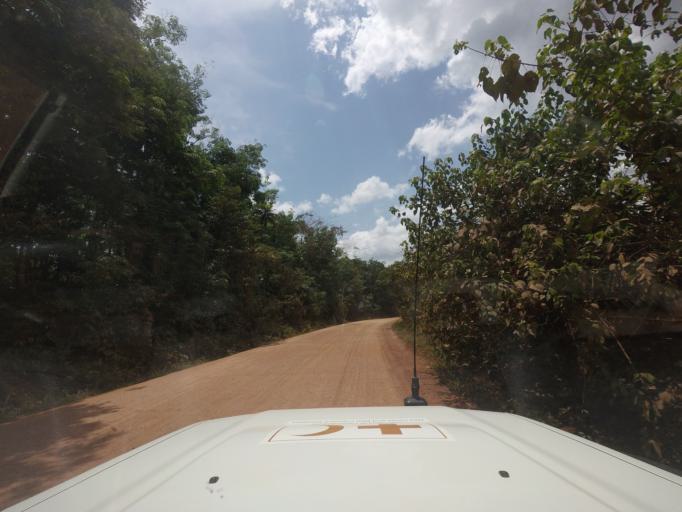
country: LR
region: Nimba
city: Sanniquellie
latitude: 7.2255
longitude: -8.9265
